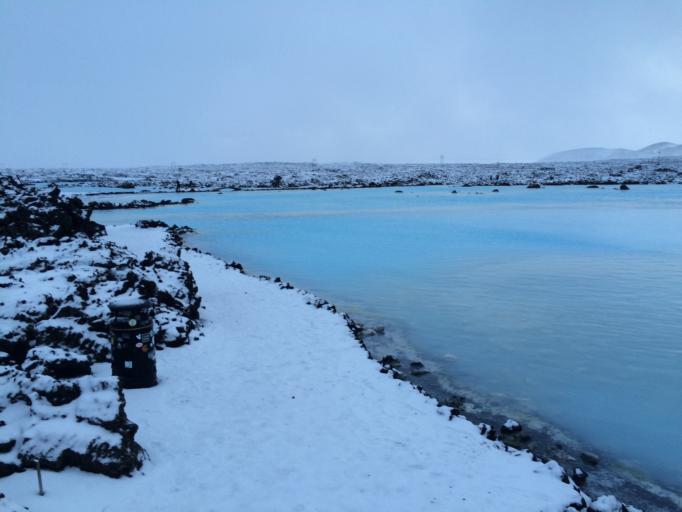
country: IS
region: Southern Peninsula
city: Grindavik
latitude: 63.8806
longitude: -22.4489
